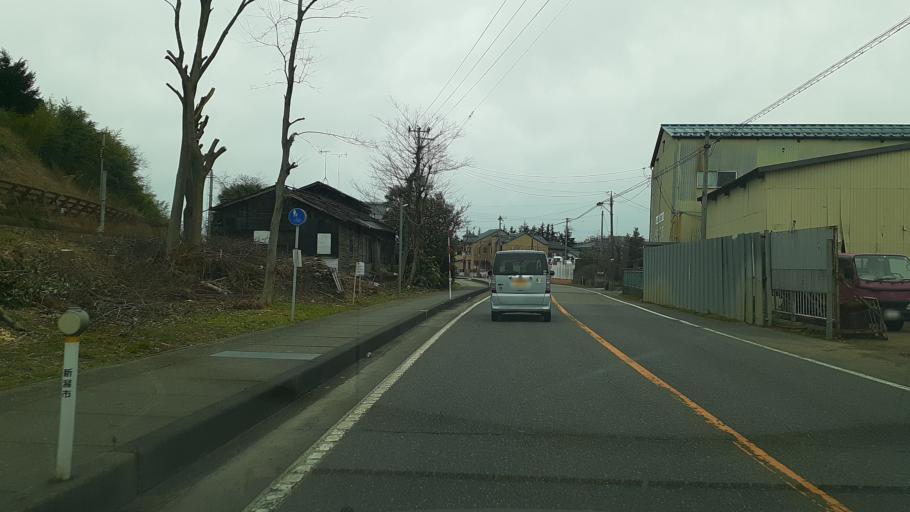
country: JP
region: Niigata
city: Niitsu-honcho
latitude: 37.7927
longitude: 139.1369
